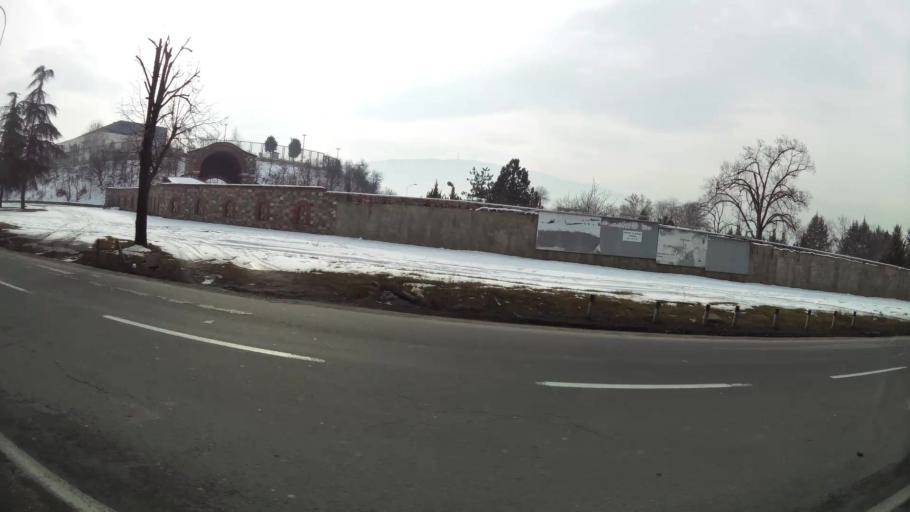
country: MK
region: Cair
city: Cair
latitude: 42.0122
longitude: 21.4258
